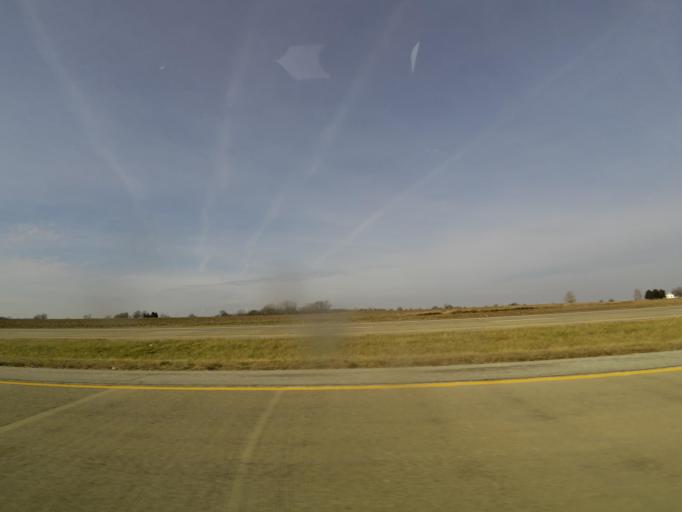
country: US
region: Illinois
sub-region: De Witt County
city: Clinton
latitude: 40.1637
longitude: -88.9813
